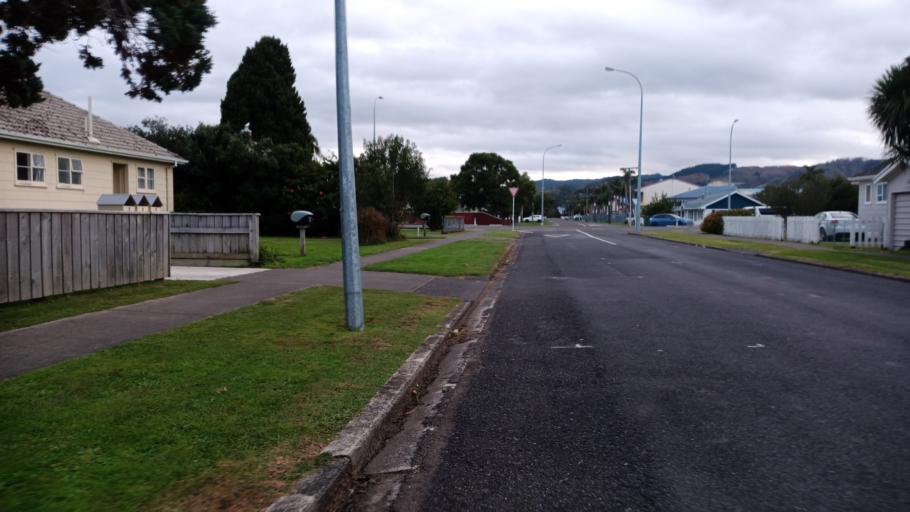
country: NZ
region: Gisborne
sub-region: Gisborne District
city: Gisborne
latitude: -38.6556
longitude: 178.0066
